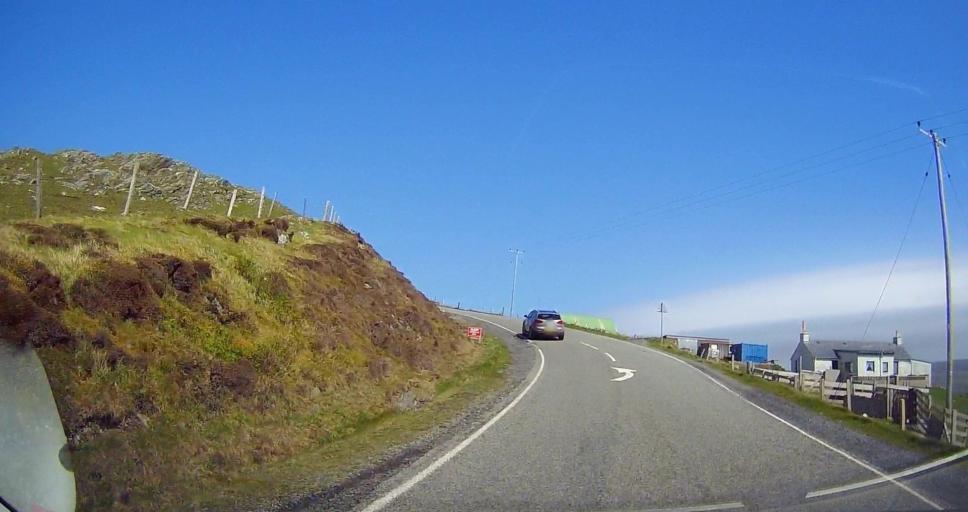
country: GB
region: Scotland
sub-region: Shetland Islands
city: Sandwick
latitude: 60.0946
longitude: -1.3222
